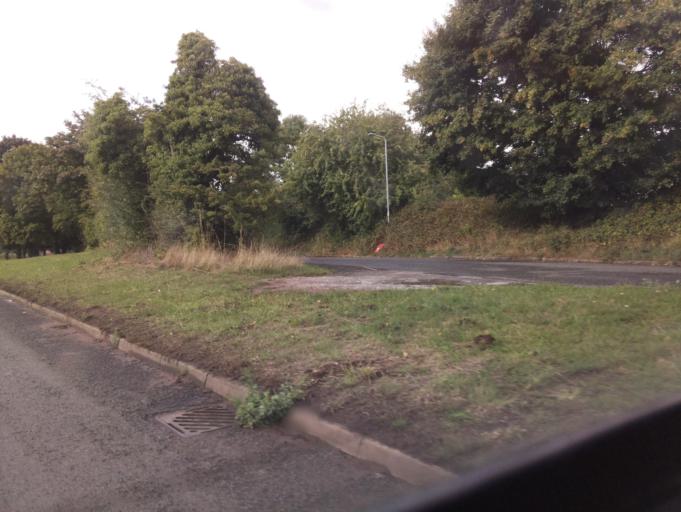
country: GB
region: England
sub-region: Worcestershire
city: Kidderminster
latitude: 52.3769
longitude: -2.2255
